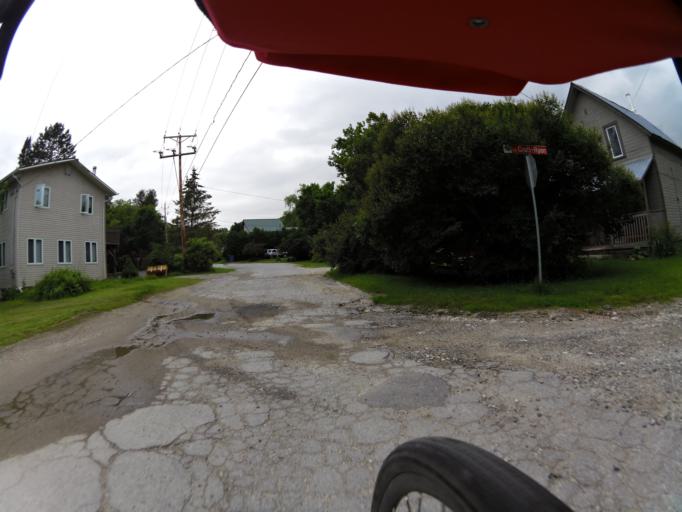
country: CA
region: Quebec
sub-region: Outaouais
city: Wakefield
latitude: 45.6830
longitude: -75.9288
